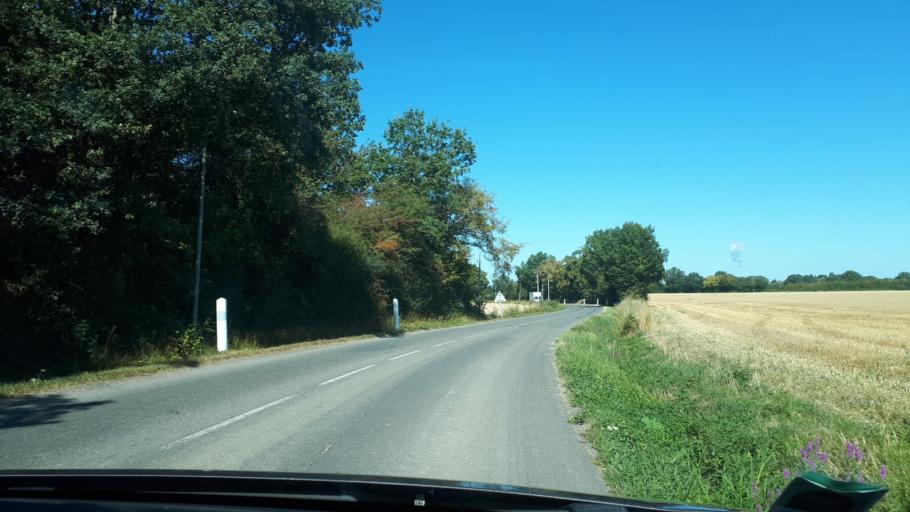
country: FR
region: Centre
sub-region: Departement du Loiret
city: Briare
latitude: 47.5934
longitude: 2.7075
